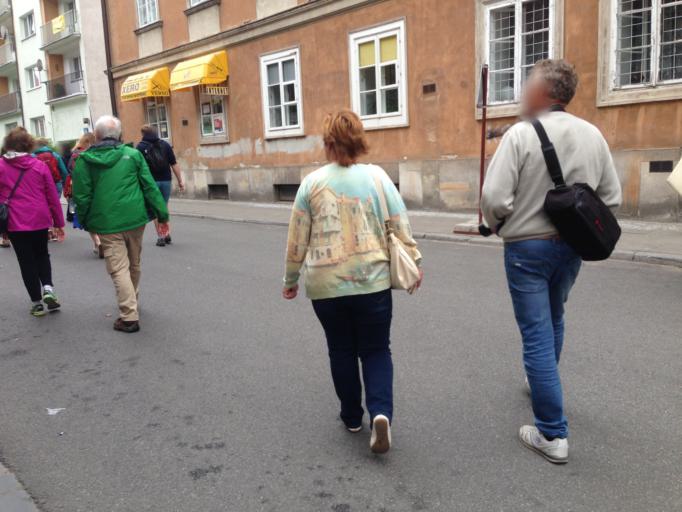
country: PL
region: Masovian Voivodeship
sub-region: Warszawa
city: Warsaw
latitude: 52.2516
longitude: 21.0084
